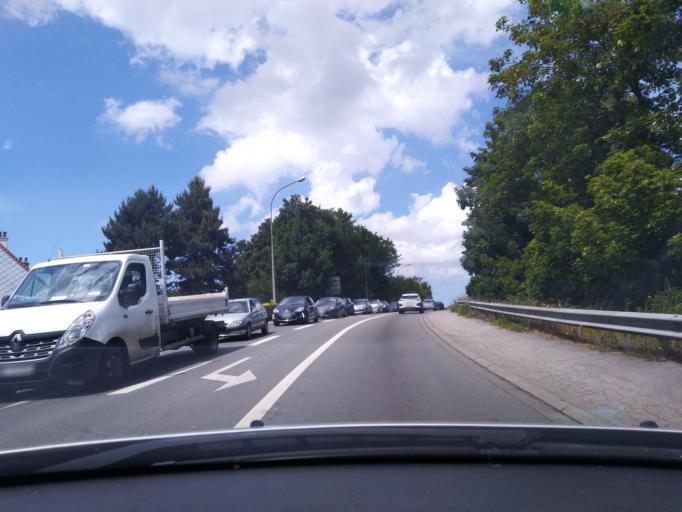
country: FR
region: Nord-Pas-de-Calais
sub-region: Departement du Pas-de-Calais
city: Saint-Etienne-au-Mont
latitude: 50.6787
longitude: 1.6335
